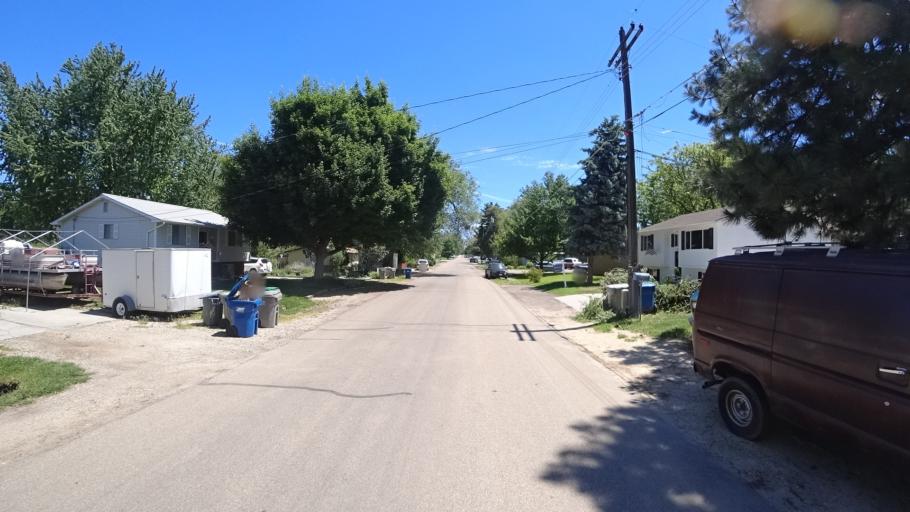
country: US
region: Idaho
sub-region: Ada County
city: Garden City
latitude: 43.5825
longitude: -116.2303
